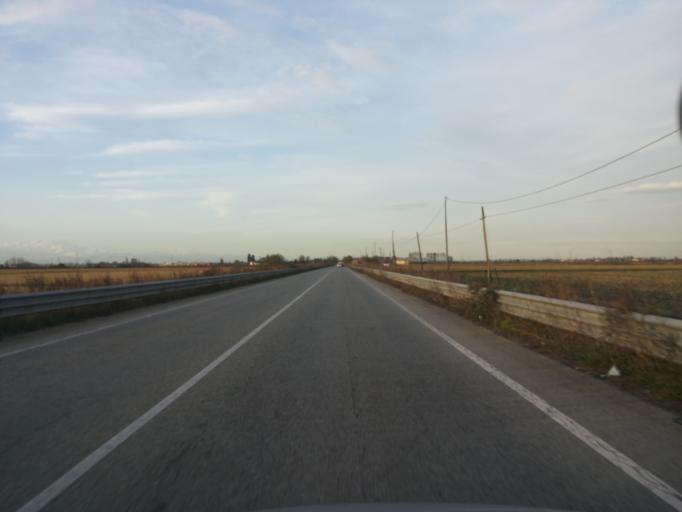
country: IT
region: Piedmont
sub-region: Provincia di Alessandria
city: Pontestura
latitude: 45.1601
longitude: 8.3319
